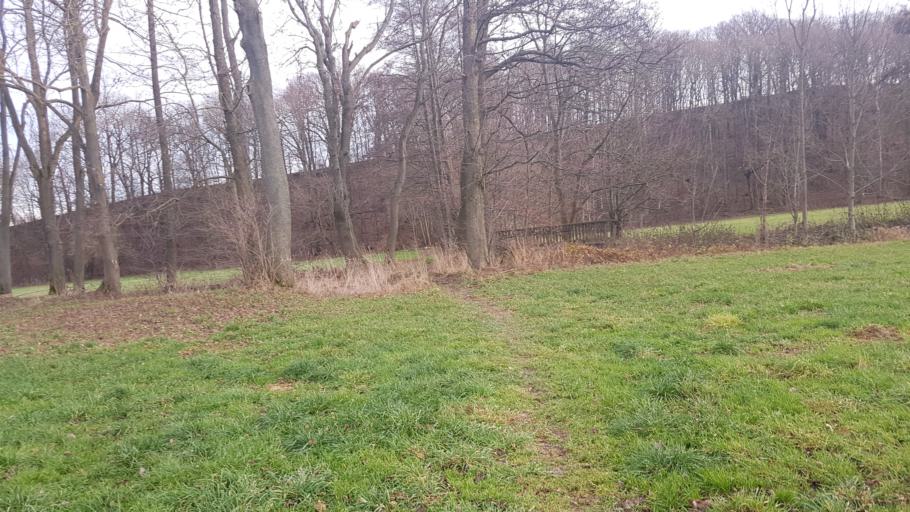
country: DE
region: Saxony
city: Ostrau
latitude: 51.1842
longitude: 13.1675
